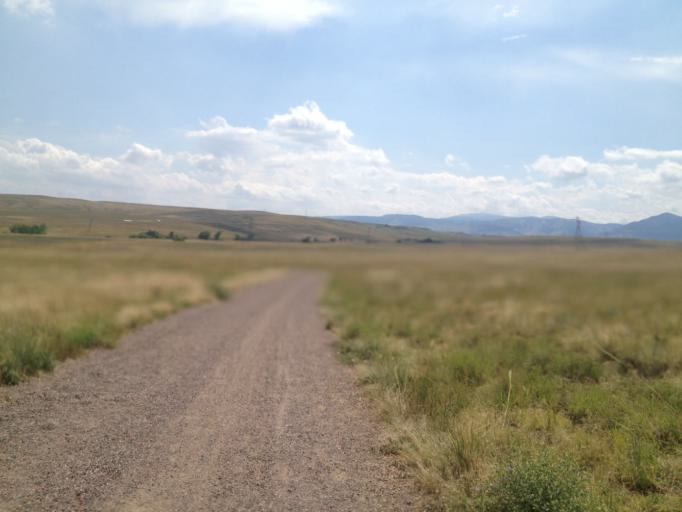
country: US
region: Colorado
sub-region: Boulder County
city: Superior
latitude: 39.9335
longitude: -105.1677
